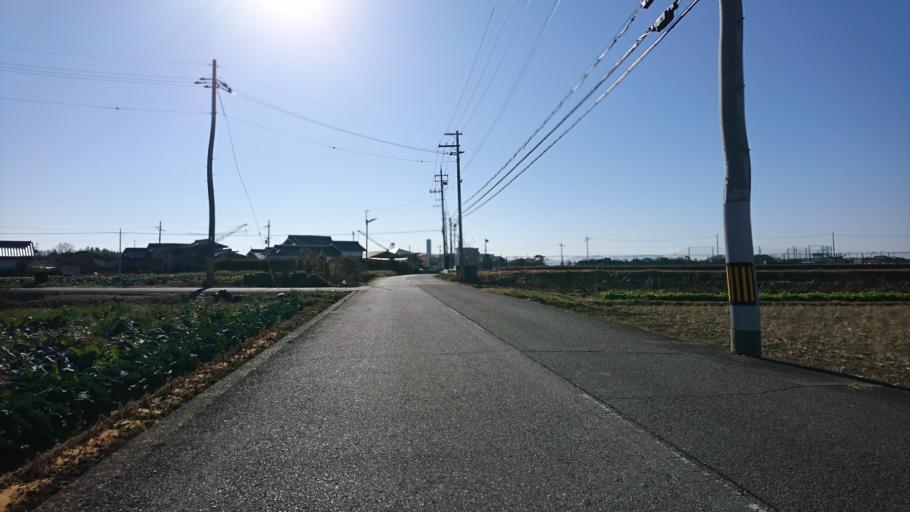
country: JP
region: Hyogo
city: Miki
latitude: 34.7195
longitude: 134.9605
